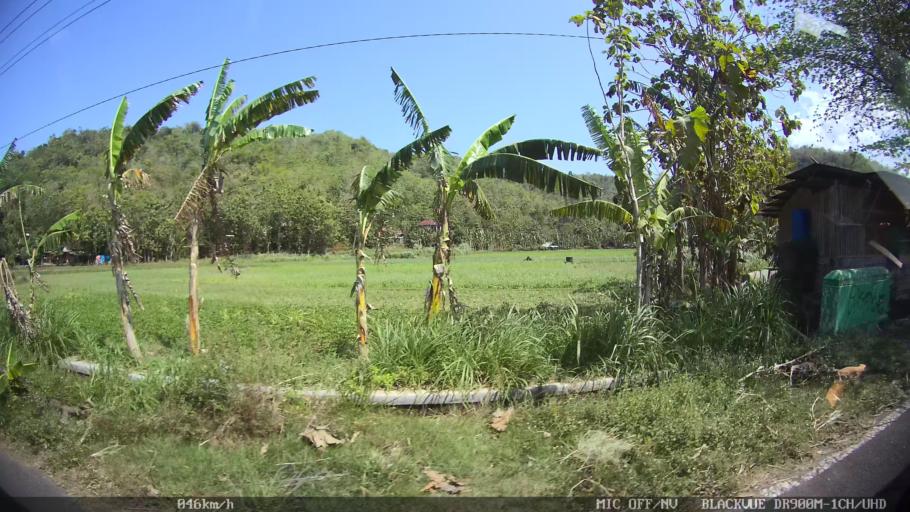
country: ID
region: Daerah Istimewa Yogyakarta
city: Pundong
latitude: -7.9572
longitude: 110.3710
